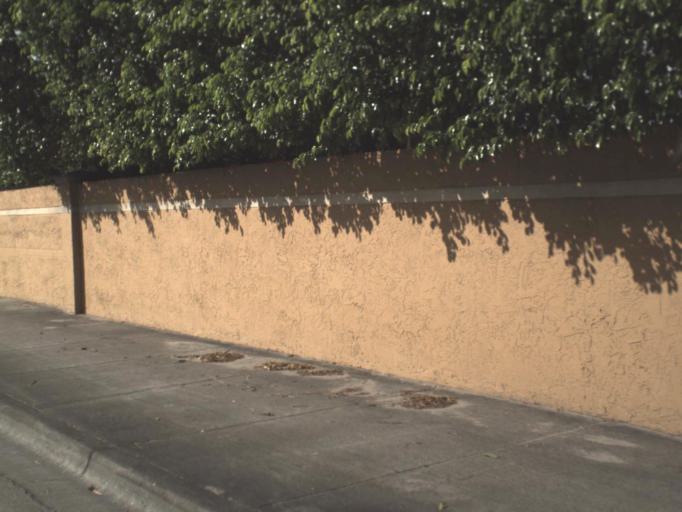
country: US
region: Florida
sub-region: Miami-Dade County
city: Three Lakes
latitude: 25.6267
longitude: -80.4021
